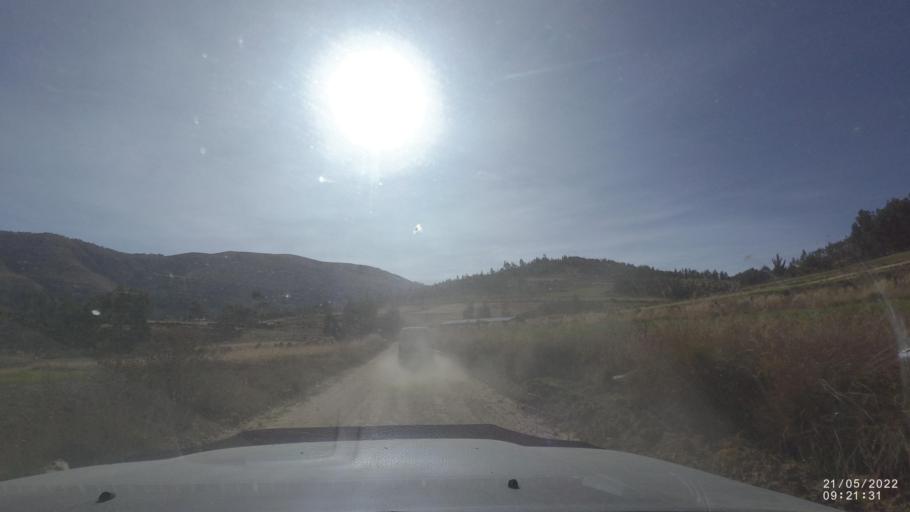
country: BO
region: Cochabamba
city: Cochabamba
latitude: -17.3522
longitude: -66.0162
